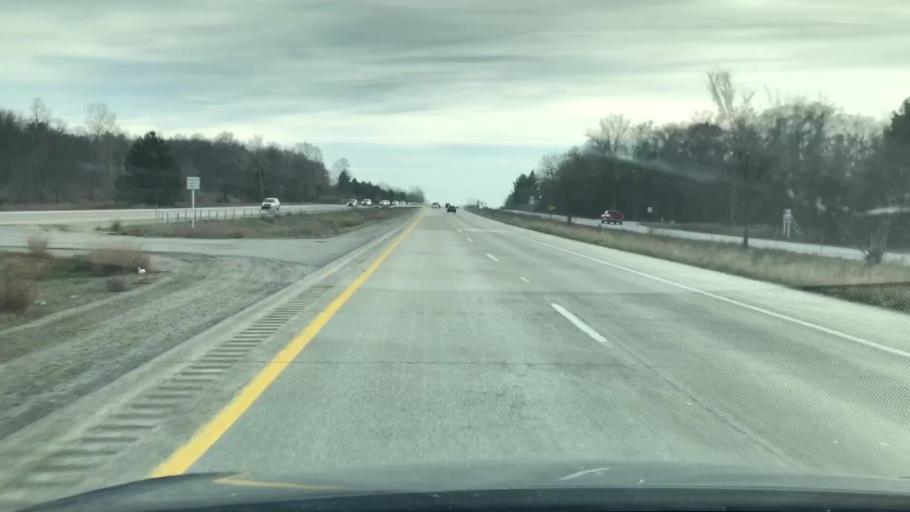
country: US
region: Michigan
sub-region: Genesee County
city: Fenton
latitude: 42.6708
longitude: -83.7598
